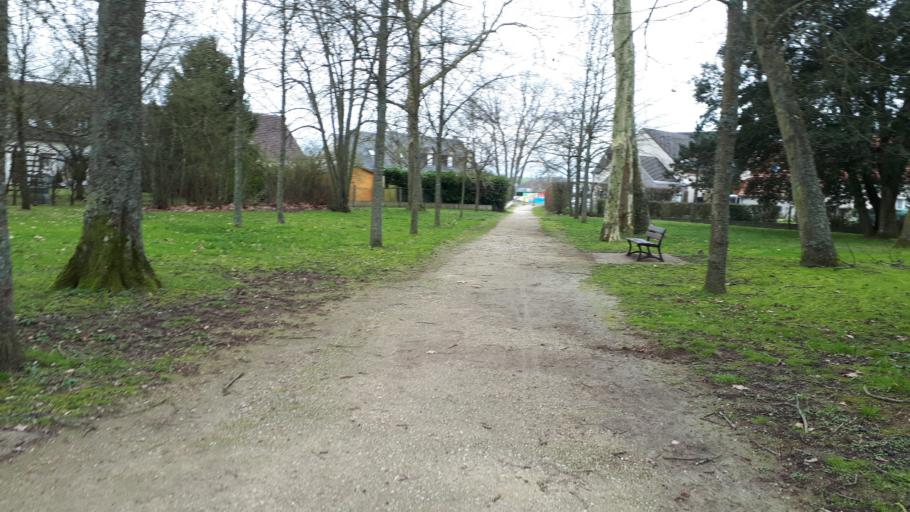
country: FR
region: Centre
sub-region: Departement du Loir-et-Cher
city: Naveil
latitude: 47.8040
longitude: 1.0420
